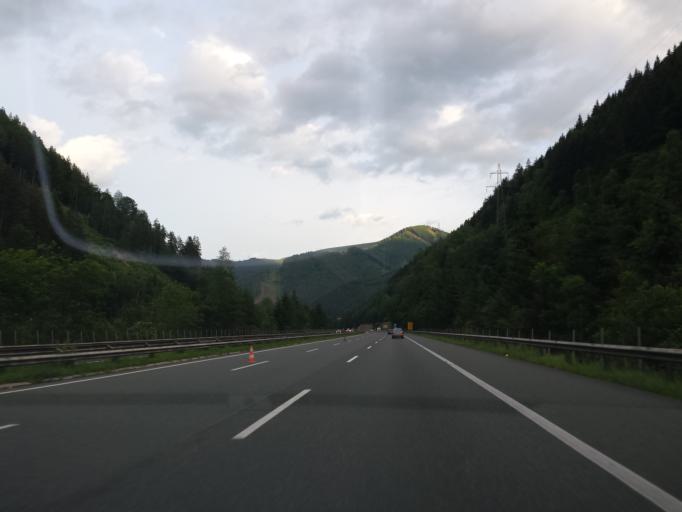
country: AT
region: Styria
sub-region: Politischer Bezirk Leoben
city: Sankt Michael in Obersteiermark
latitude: 47.3086
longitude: 15.0583
